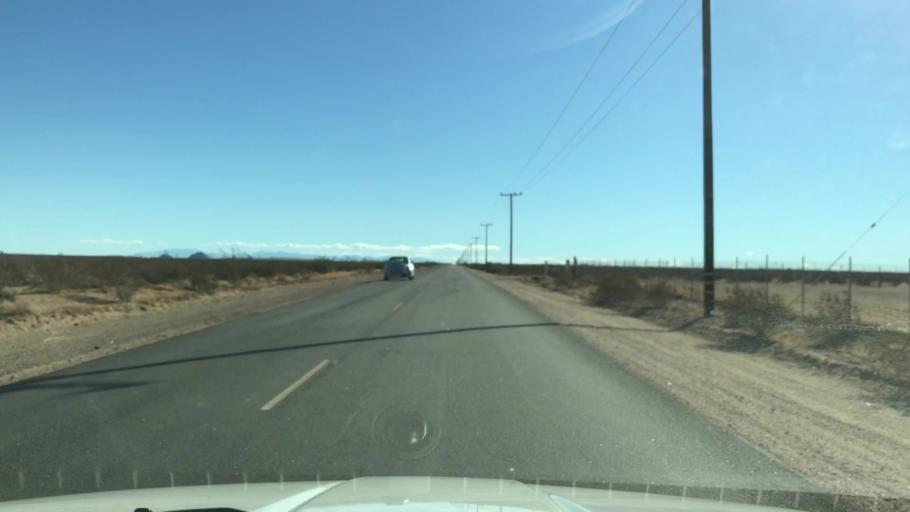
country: US
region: California
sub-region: Kern County
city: California City
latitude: 35.2203
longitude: -117.9859
